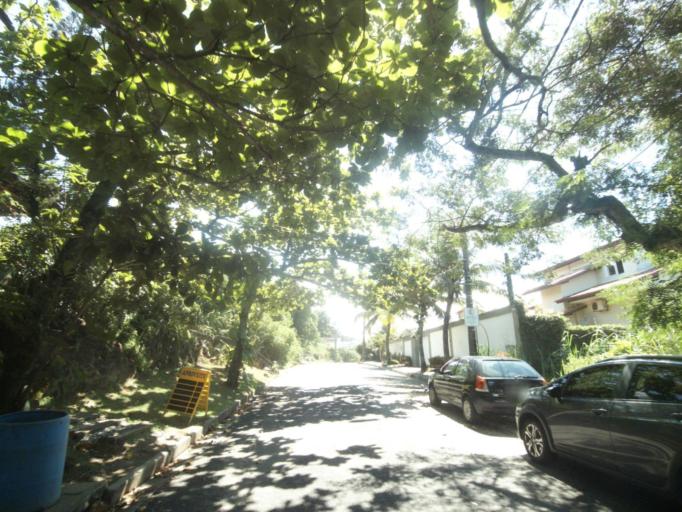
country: BR
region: Rio de Janeiro
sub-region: Niteroi
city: Niteroi
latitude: -22.9580
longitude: -43.0684
